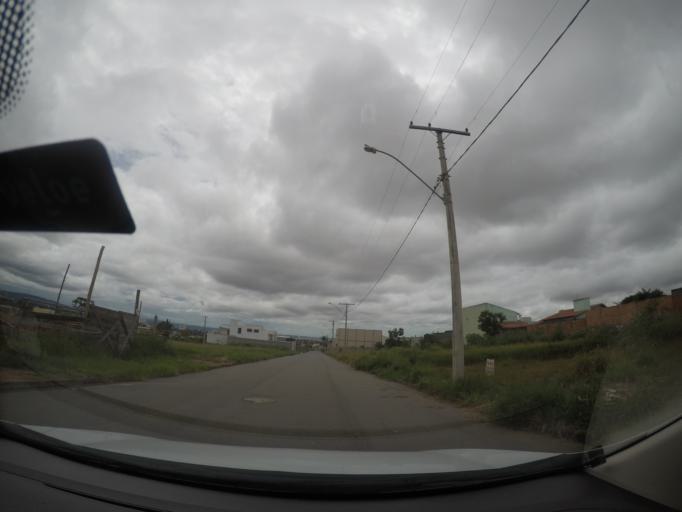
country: BR
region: Goias
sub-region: Goiania
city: Goiania
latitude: -16.7470
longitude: -49.3362
